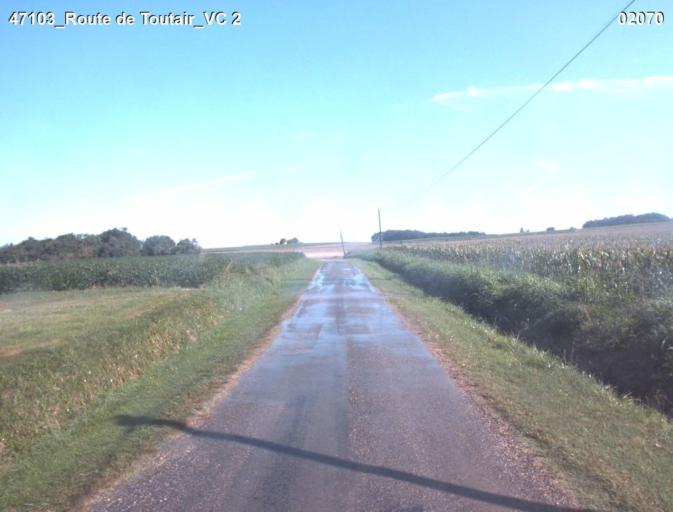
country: FR
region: Aquitaine
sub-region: Departement du Lot-et-Garonne
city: Nerac
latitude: 44.0707
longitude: 0.3339
